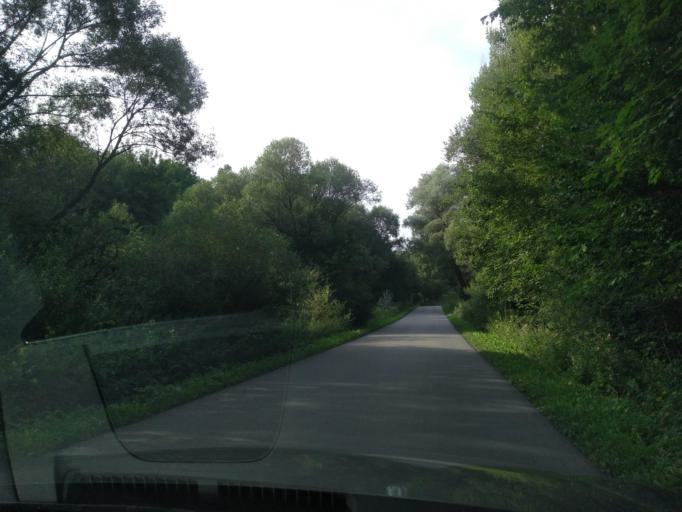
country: PL
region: Subcarpathian Voivodeship
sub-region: Powiat brzozowski
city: Dydnia
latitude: 49.6486
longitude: 22.2317
